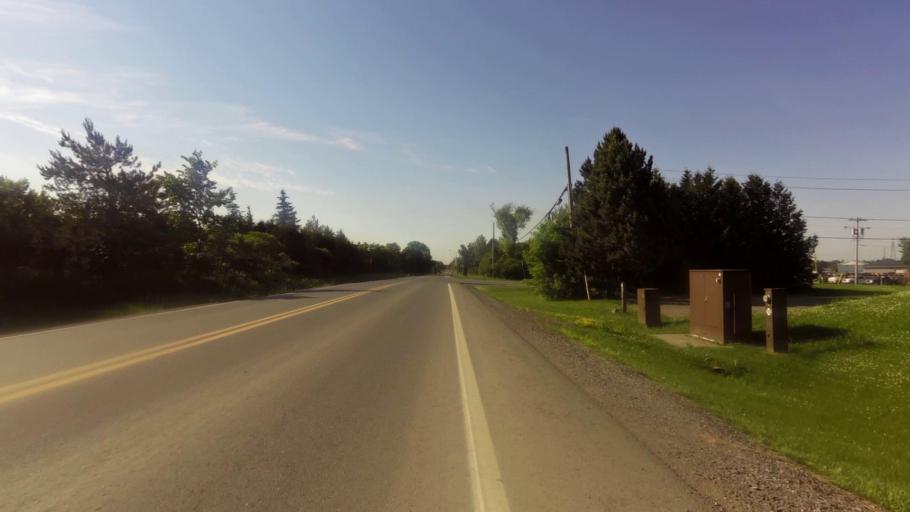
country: CA
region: Ontario
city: Ottawa
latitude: 45.2622
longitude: -75.5705
